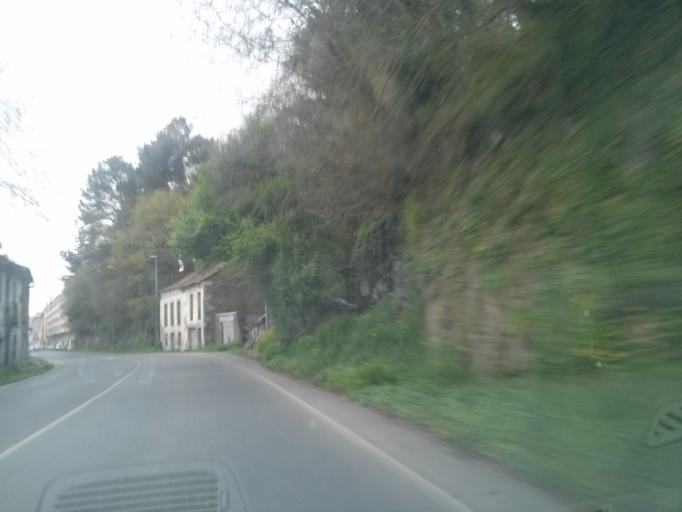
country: ES
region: Galicia
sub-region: Provincia de Lugo
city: Lugo
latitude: 43.0205
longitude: -7.5475
